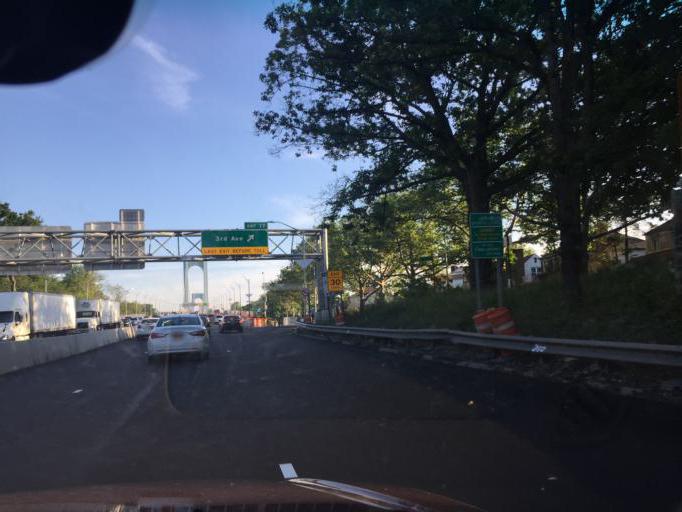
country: US
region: New York
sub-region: Bronx
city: The Bronx
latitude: 40.7927
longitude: -73.8237
